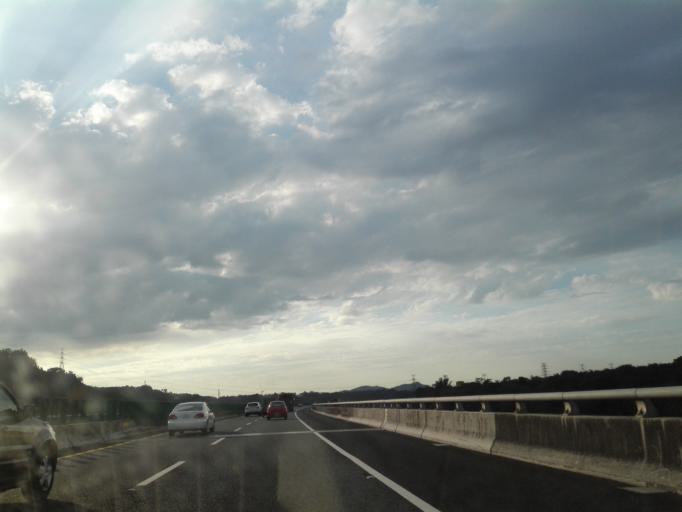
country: TW
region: Taiwan
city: Zhongxing New Village
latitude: 23.9823
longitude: 120.7683
